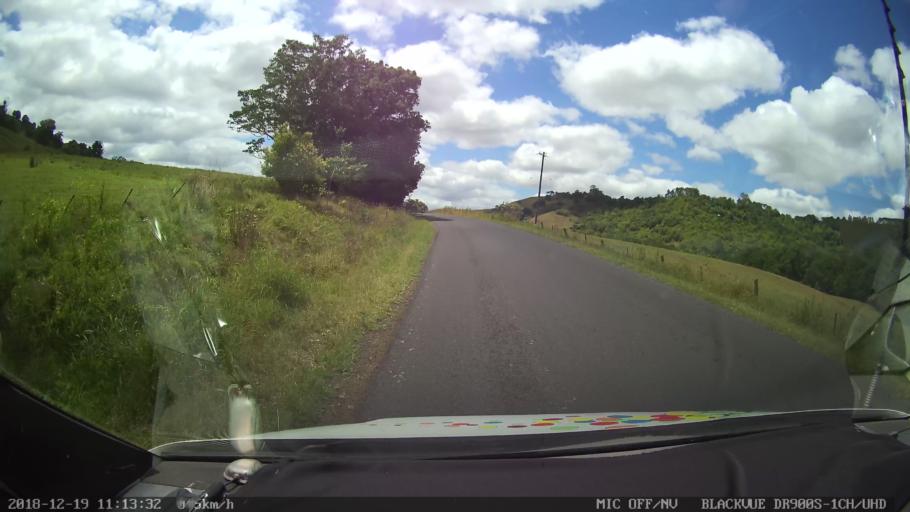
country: AU
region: New South Wales
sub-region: Lismore Municipality
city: Nimbin
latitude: -28.6563
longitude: 153.2641
